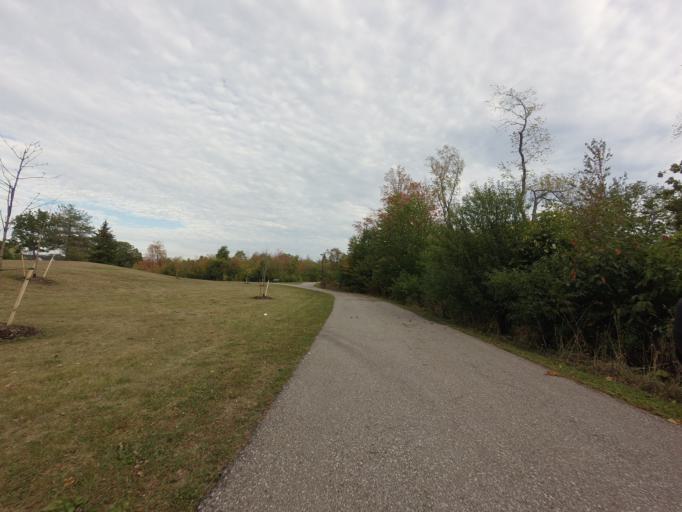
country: CA
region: Ontario
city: Mississauga
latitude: 43.5365
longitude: -79.6750
